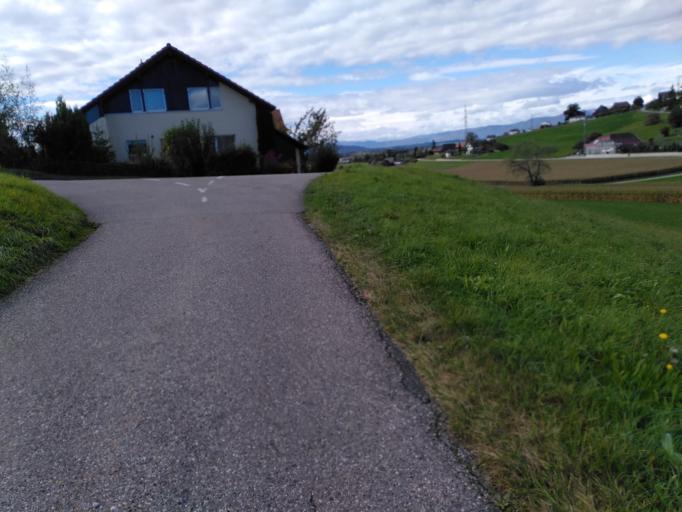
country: CH
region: Bern
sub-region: Emmental District
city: Wynigen
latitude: 47.1232
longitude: 7.6377
